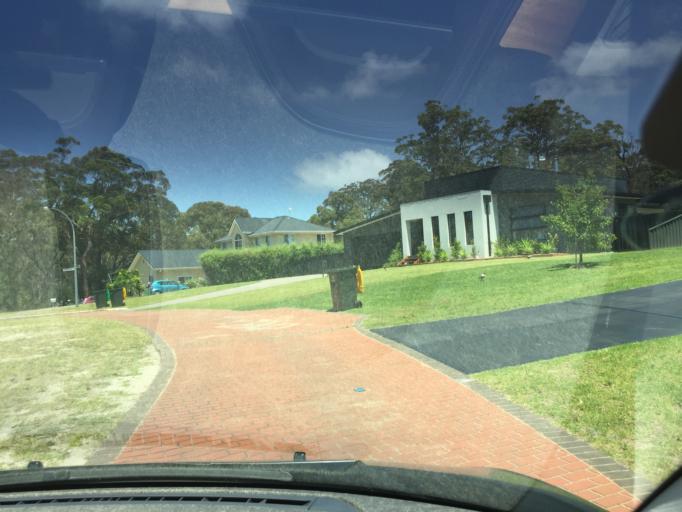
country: AU
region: New South Wales
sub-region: Bega Valley
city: Merimbula
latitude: -36.8531
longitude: 149.9250
